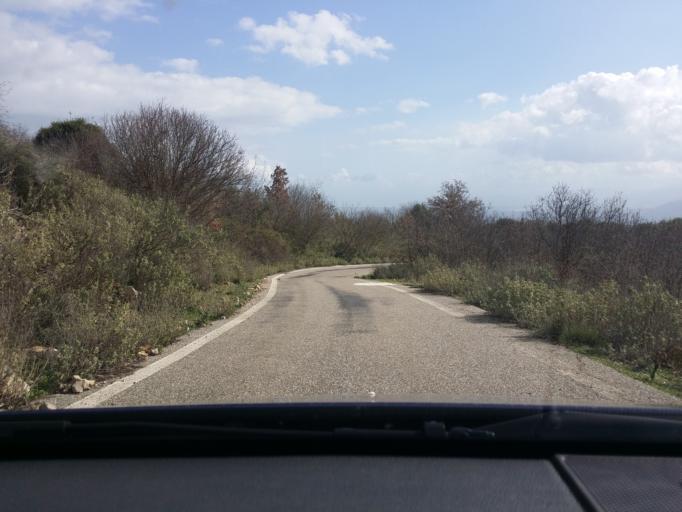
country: GR
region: West Greece
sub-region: Nomos Aitolias kai Akarnanias
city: Fitiai
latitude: 38.6444
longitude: 21.1967
